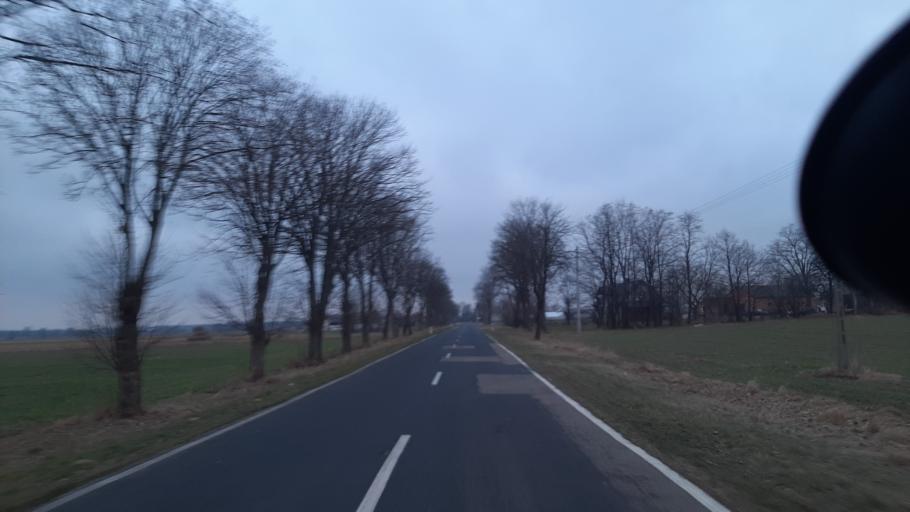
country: PL
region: Lublin Voivodeship
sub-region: Powiat parczewski
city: Debowa Kloda
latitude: 51.6346
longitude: 23.0682
